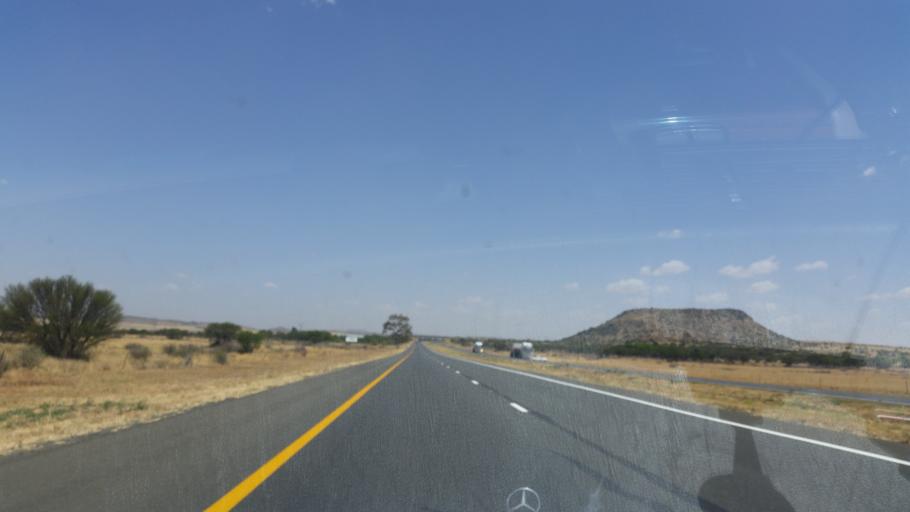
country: ZA
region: Orange Free State
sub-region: Lejweleputswa District Municipality
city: Brandfort
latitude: -28.9465
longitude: 26.4019
